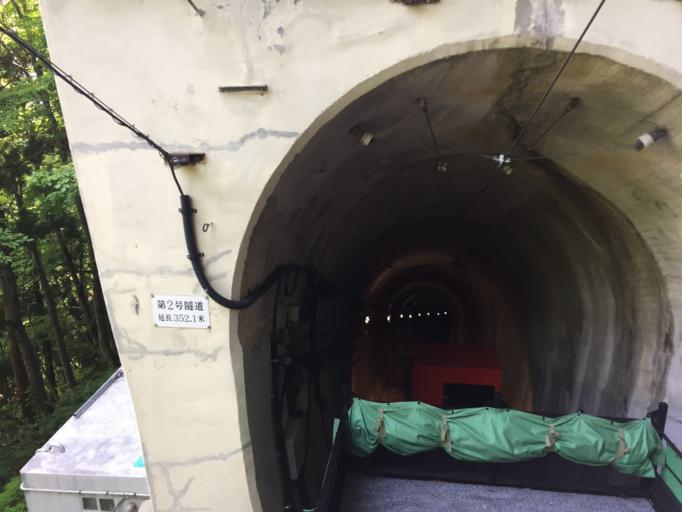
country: JP
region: Toyama
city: Kamiichi
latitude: 36.5822
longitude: 137.4561
